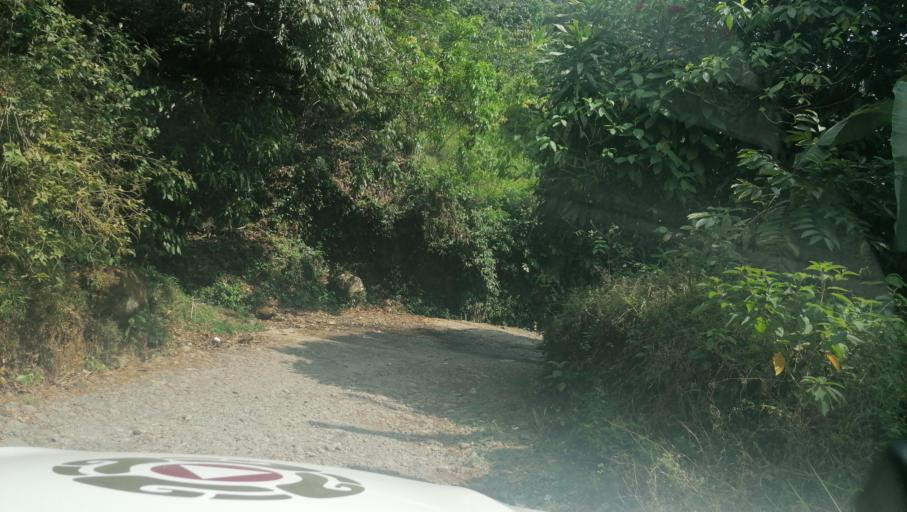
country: MX
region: Chiapas
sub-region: Cacahoatan
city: Benito Juarez
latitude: 15.0384
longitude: -92.2362
